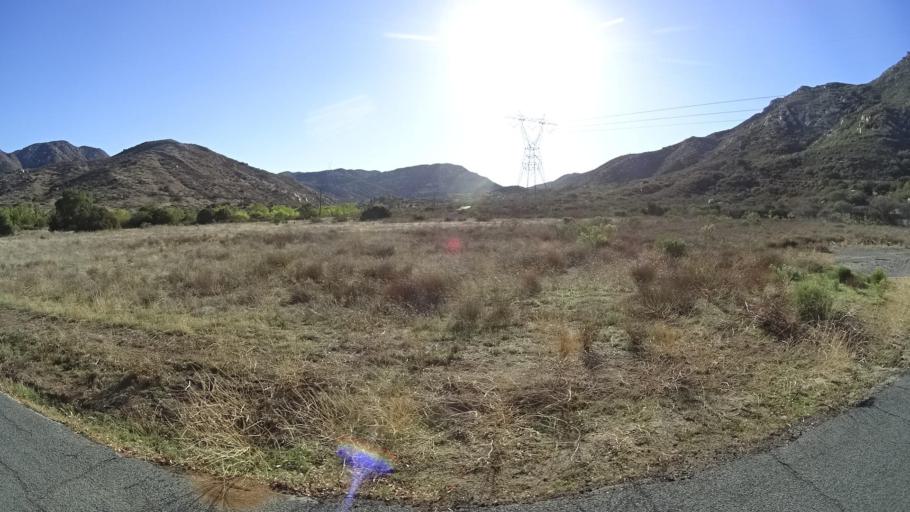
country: MX
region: Baja California
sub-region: Tecate
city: Lomas de Santa Anita
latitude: 32.6063
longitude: -116.6958
